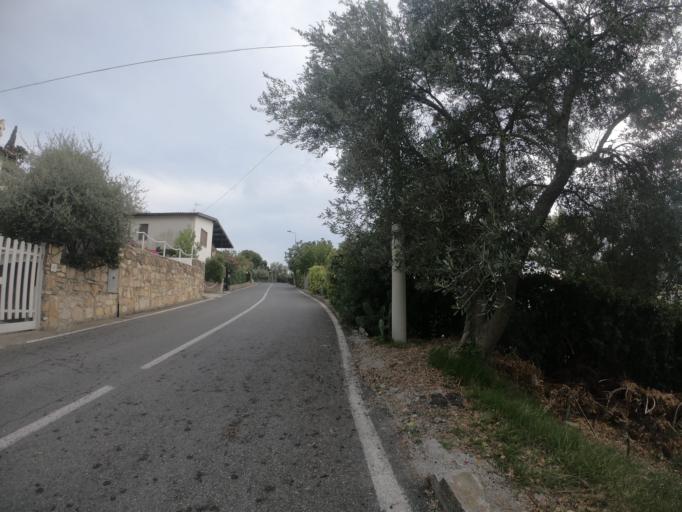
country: IT
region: Liguria
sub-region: Provincia di Savona
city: Marina di Andora
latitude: 43.9546
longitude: 8.1520
